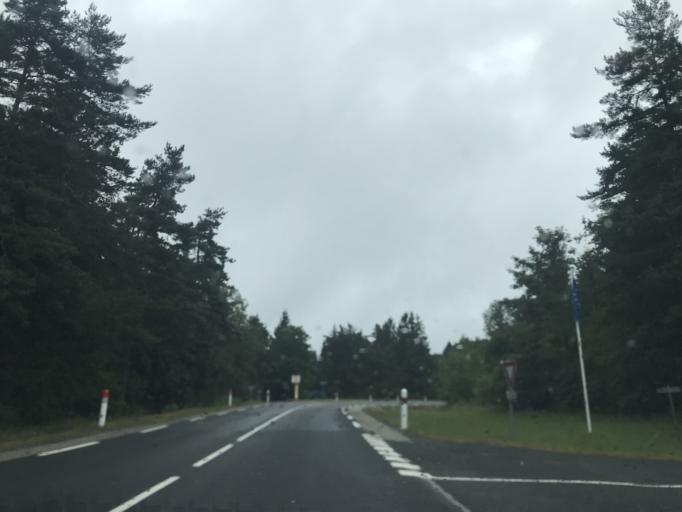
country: FR
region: Auvergne
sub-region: Departement de la Haute-Loire
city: Fontannes
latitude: 45.3352
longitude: 3.7039
